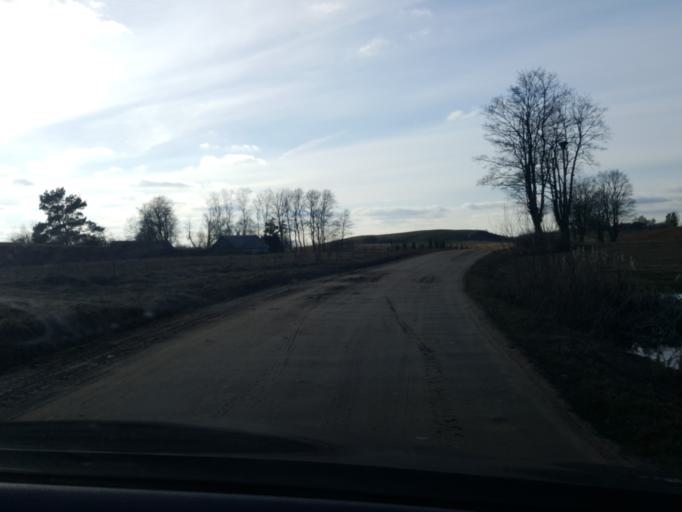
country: LT
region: Alytaus apskritis
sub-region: Alytus
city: Alytus
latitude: 54.3427
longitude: 23.8689
